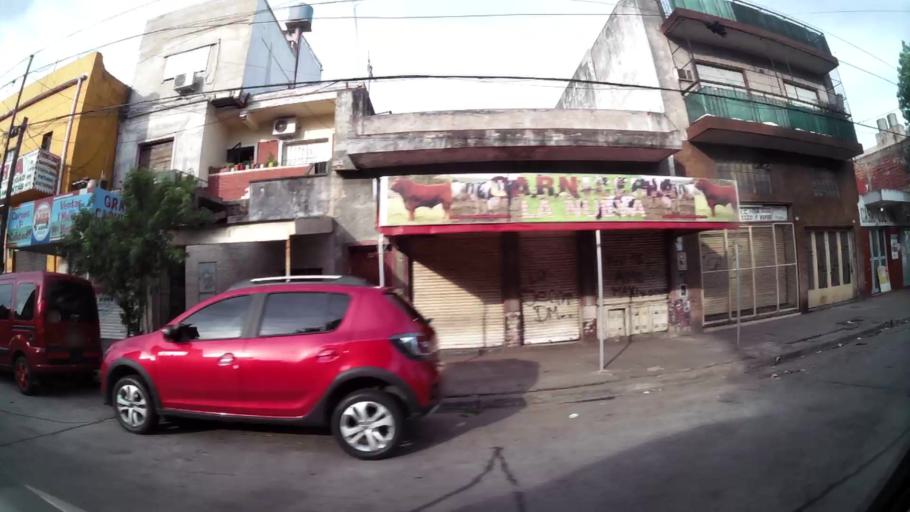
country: AR
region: Buenos Aires F.D.
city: Villa Lugano
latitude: -34.6440
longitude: -58.4409
